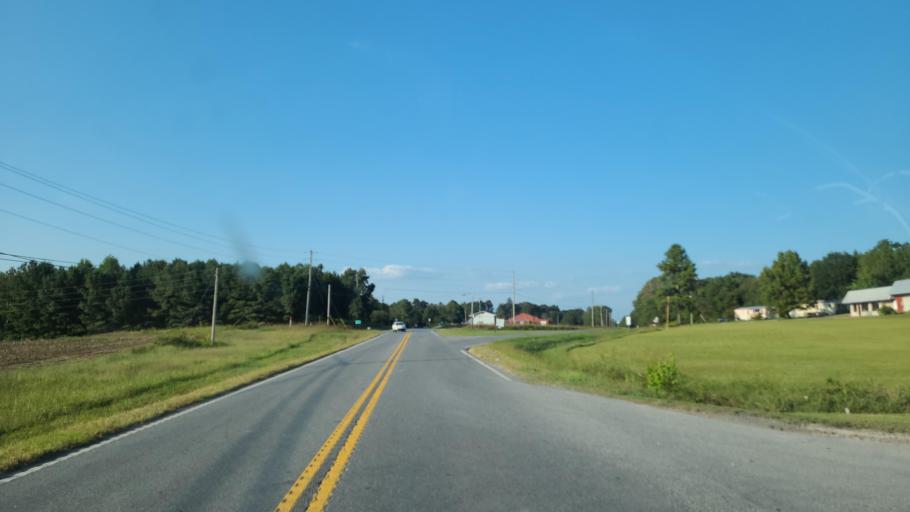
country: US
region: Tennessee
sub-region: Bradley County
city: Wildwood Lake
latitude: 34.9596
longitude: -84.7736
